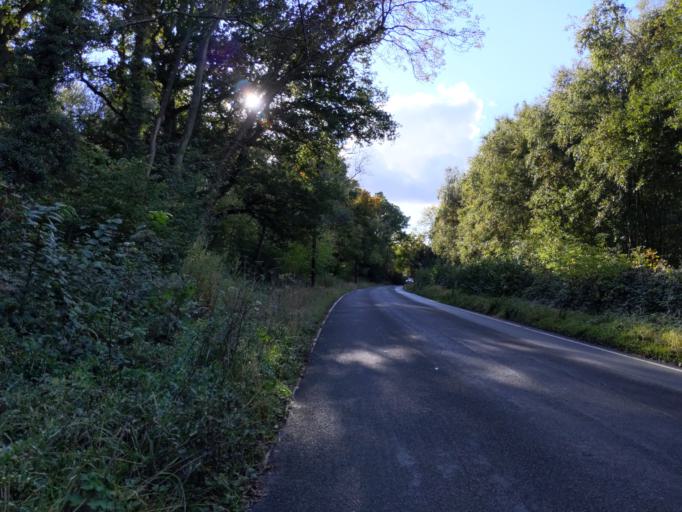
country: GB
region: England
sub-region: Oxfordshire
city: Radley
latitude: 51.7100
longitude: -1.2514
